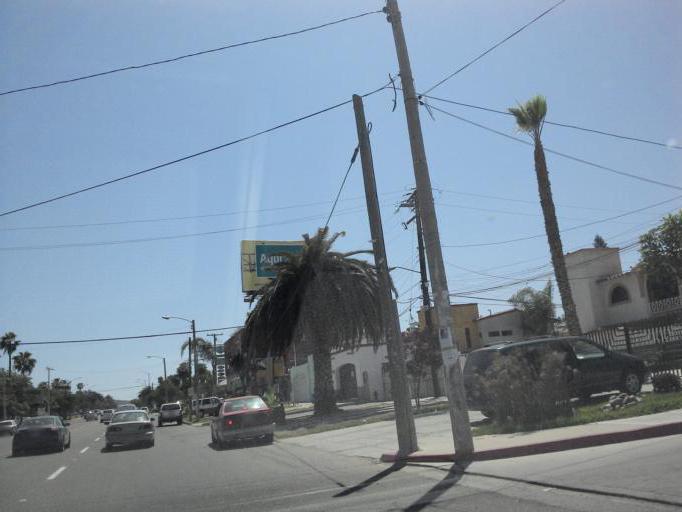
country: US
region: California
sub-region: San Diego County
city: Imperial Beach
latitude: 32.5295
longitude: -117.1163
